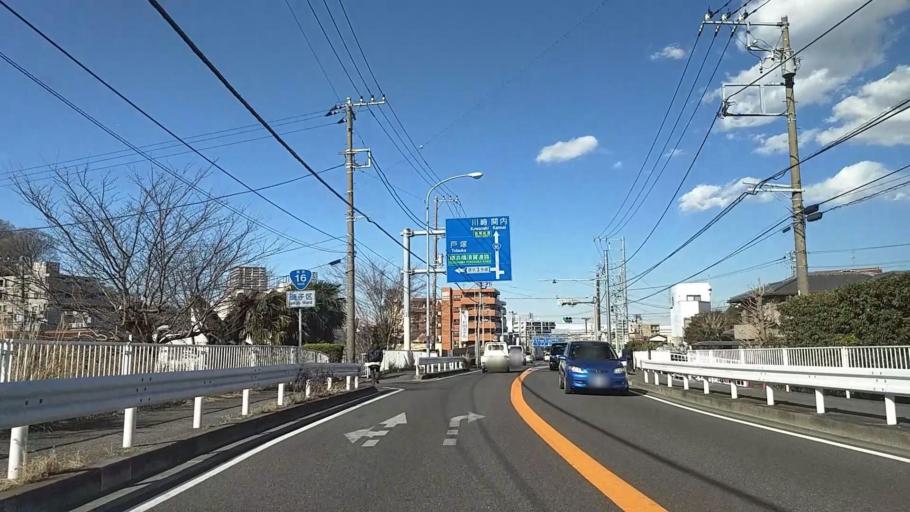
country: JP
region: Kanagawa
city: Yokohama
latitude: 35.3781
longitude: 139.6219
